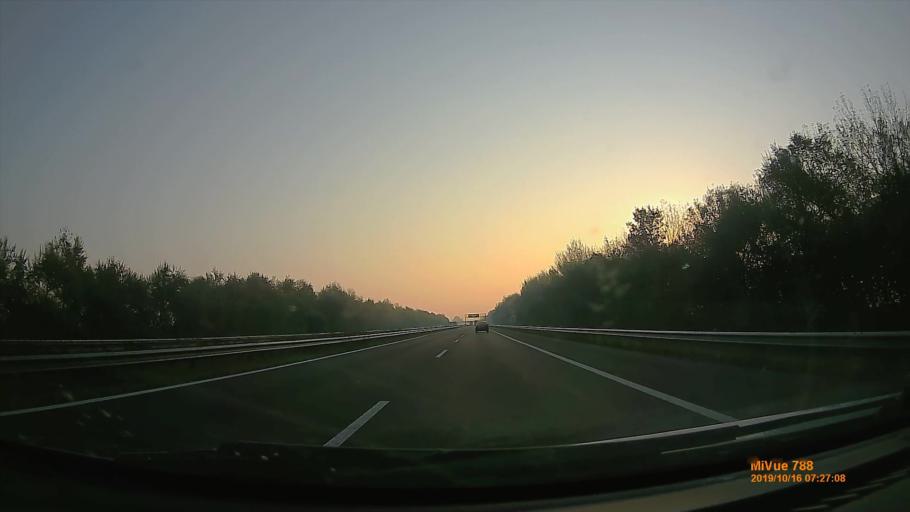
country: HU
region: Heves
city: Fuzesabony
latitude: 47.7296
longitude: 20.3881
